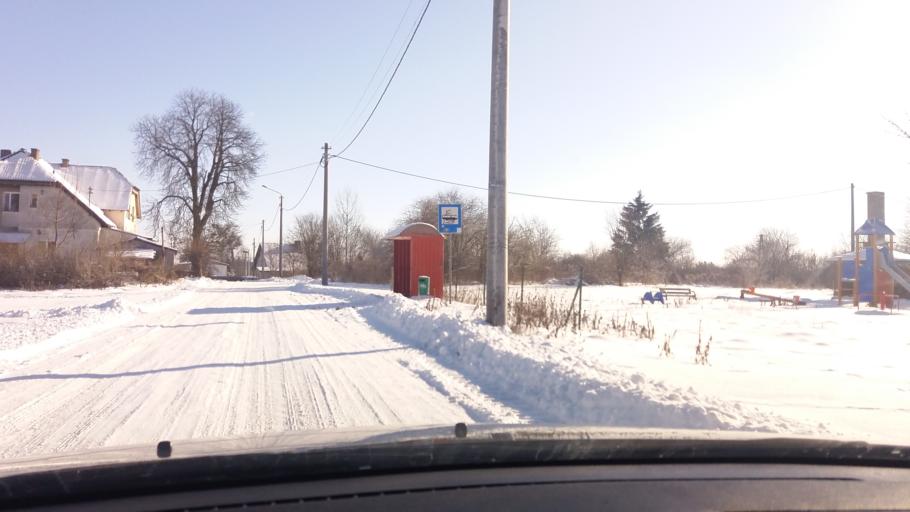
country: PL
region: Warmian-Masurian Voivodeship
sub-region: Powiat szczycienski
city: Szczytno
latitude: 53.5488
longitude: 20.9848
